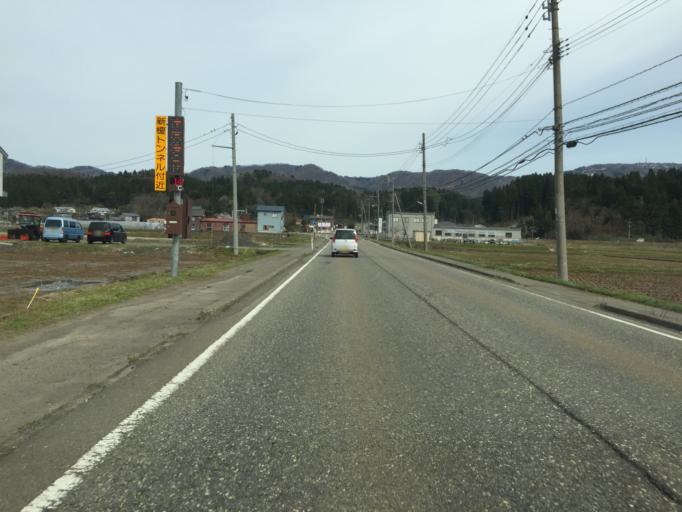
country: JP
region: Niigata
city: Nagaoka
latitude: 37.4540
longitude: 138.8932
